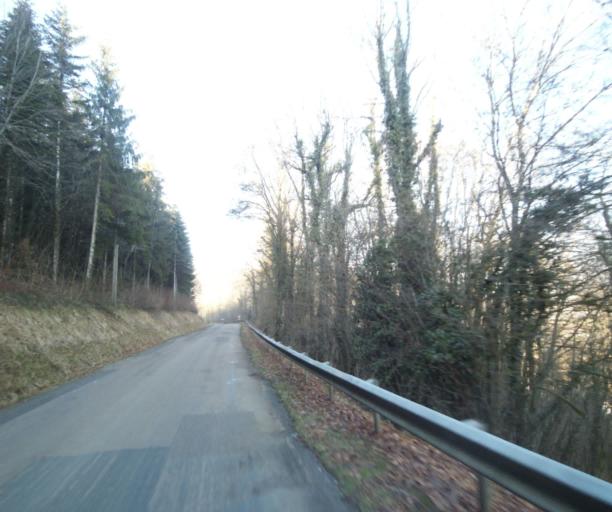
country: FR
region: Champagne-Ardenne
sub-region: Departement de la Haute-Marne
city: Chevillon
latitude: 48.5217
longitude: 5.0914
